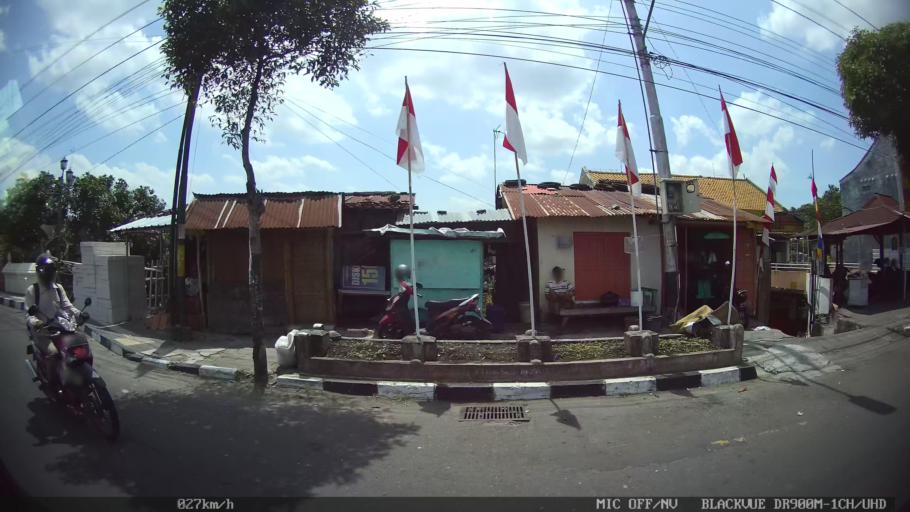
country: ID
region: Daerah Istimewa Yogyakarta
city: Yogyakarta
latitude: -7.8084
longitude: 110.3543
